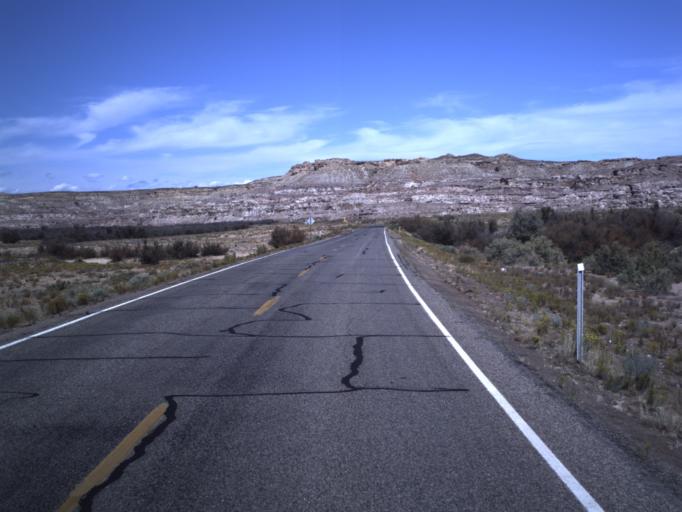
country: US
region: Utah
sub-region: San Juan County
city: Blanding
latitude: 37.2475
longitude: -109.2549
